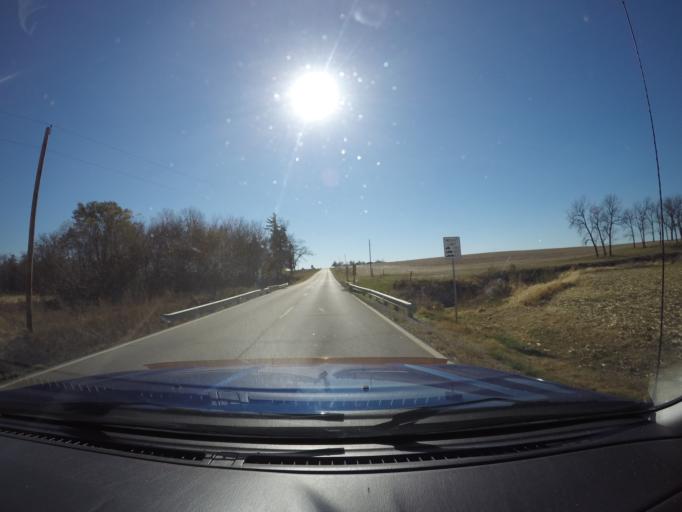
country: US
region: Kansas
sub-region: Nemaha County
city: Seneca
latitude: 39.8642
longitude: -96.2584
